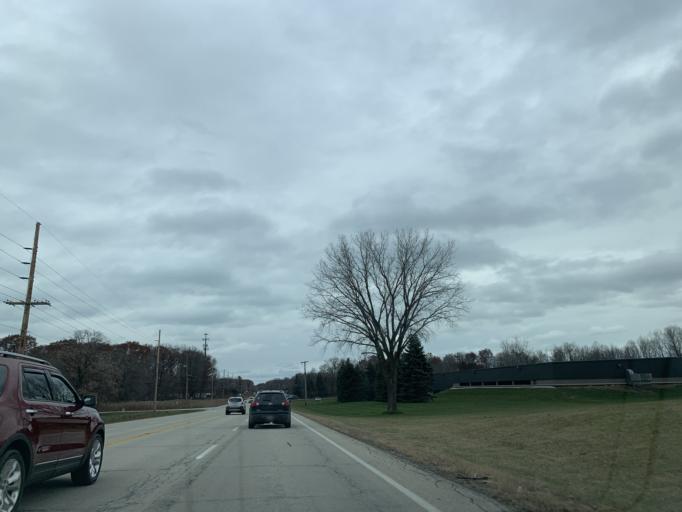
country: US
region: Indiana
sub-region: LaPorte County
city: Long Beach
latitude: 41.7313
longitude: -86.8261
